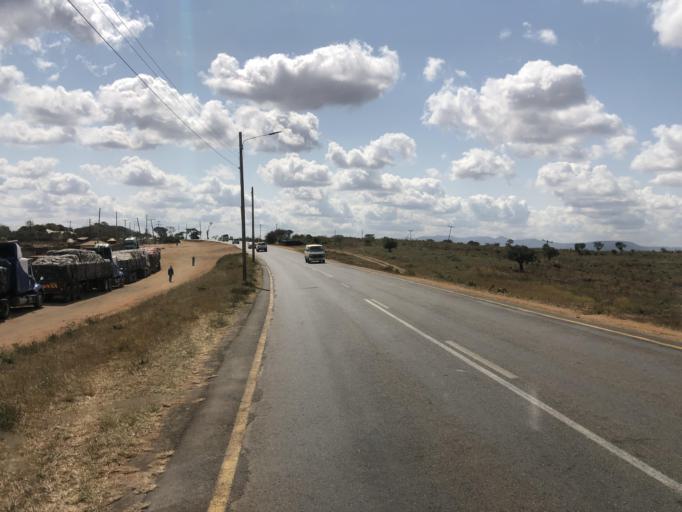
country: MW
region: Central Region
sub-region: Lilongwe District
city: Lilongwe
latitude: -13.8228
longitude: 33.8075
